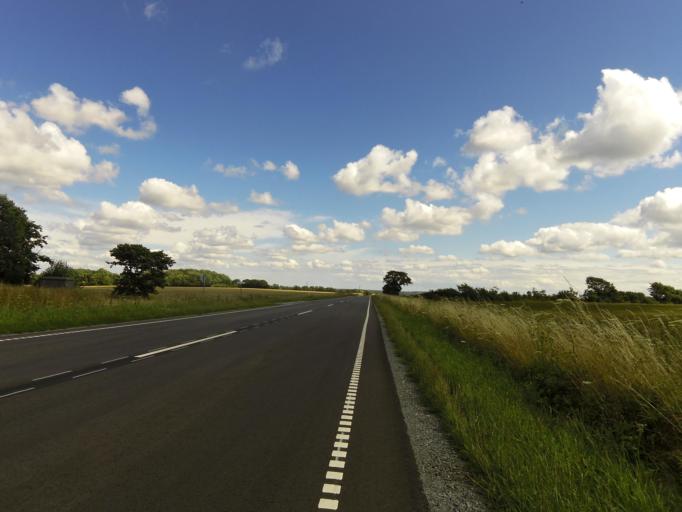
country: DK
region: South Denmark
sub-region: Haderslev Kommune
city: Gram
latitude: 55.3129
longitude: 9.1206
